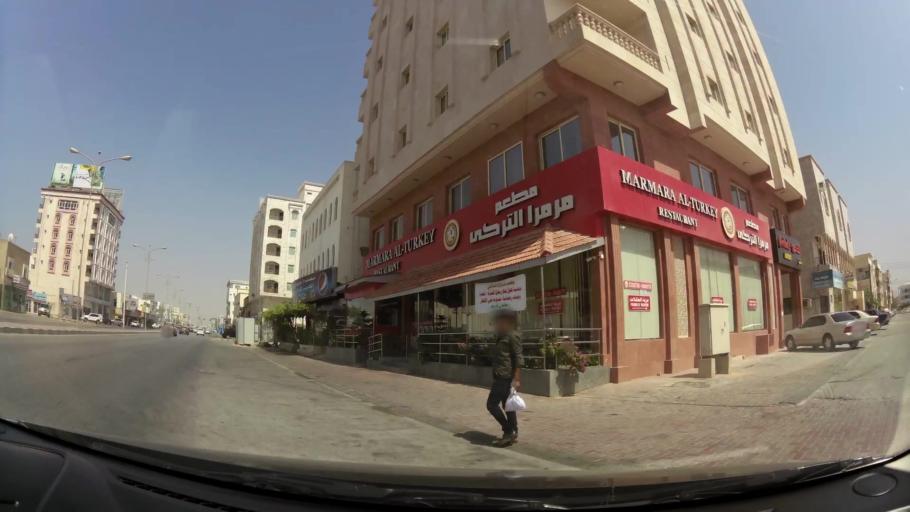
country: OM
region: Zufar
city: Salalah
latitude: 17.0191
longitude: 54.1086
